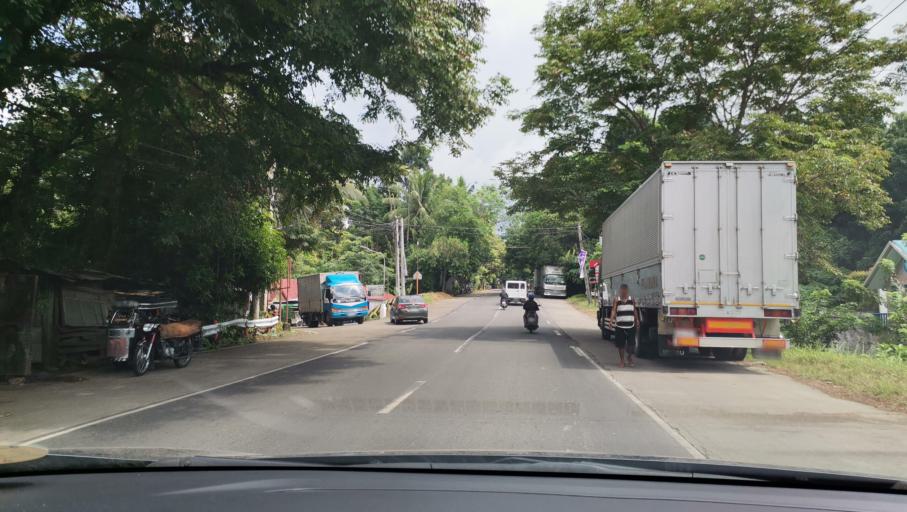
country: PH
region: Calabarzon
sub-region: Province of Quezon
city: Rizal
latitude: 13.9513
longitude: 122.2887
